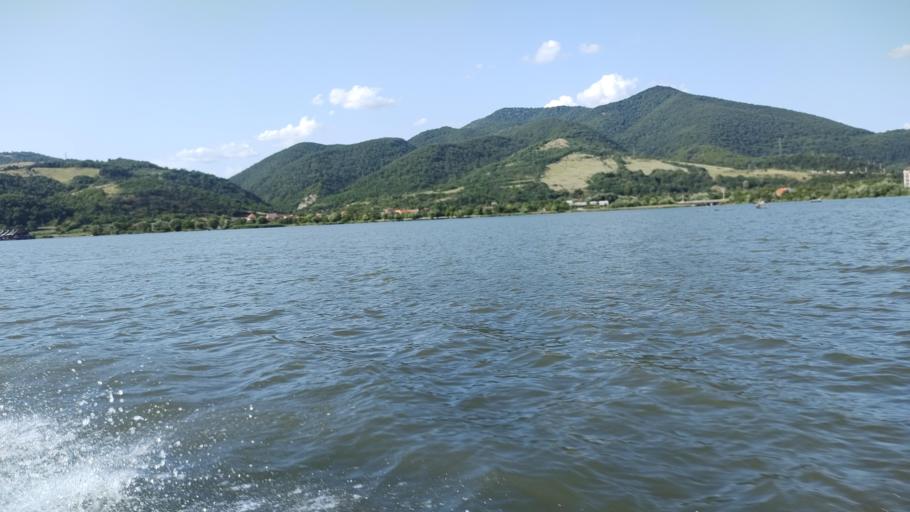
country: RO
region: Caras-Severin
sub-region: Comuna Berzasca
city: Berzasca
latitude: 44.6416
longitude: 21.9441
